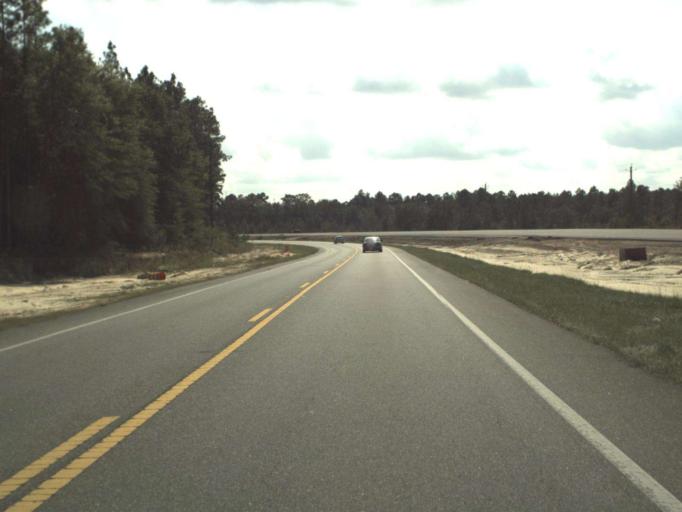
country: US
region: Florida
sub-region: Holmes County
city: Bonifay
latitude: 30.6605
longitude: -85.6982
